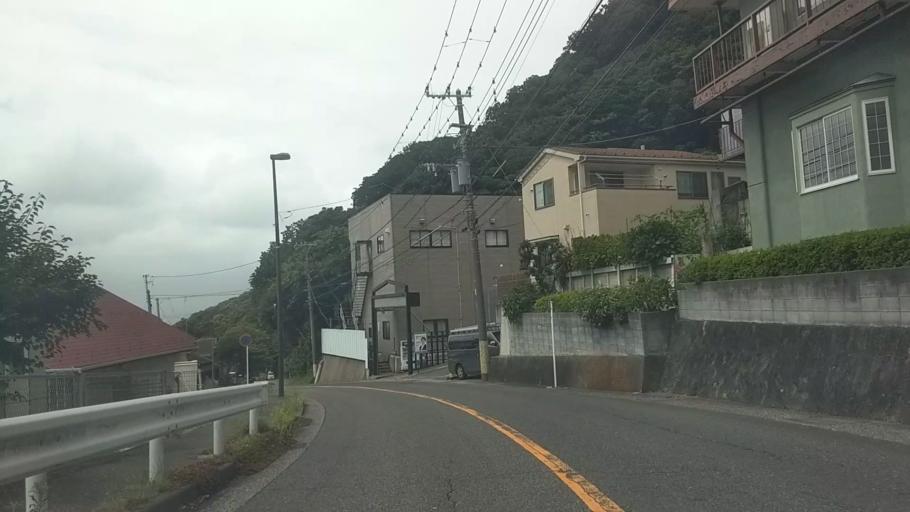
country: JP
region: Kanagawa
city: Yokosuka
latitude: 35.2578
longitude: 139.7190
